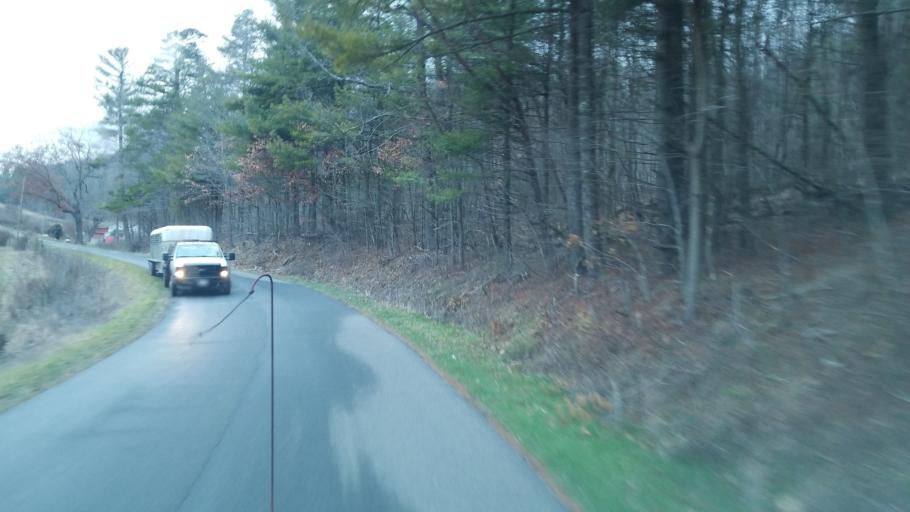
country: US
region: Virginia
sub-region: Pulaski County
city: Pulaski
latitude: 37.1836
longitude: -80.8429
